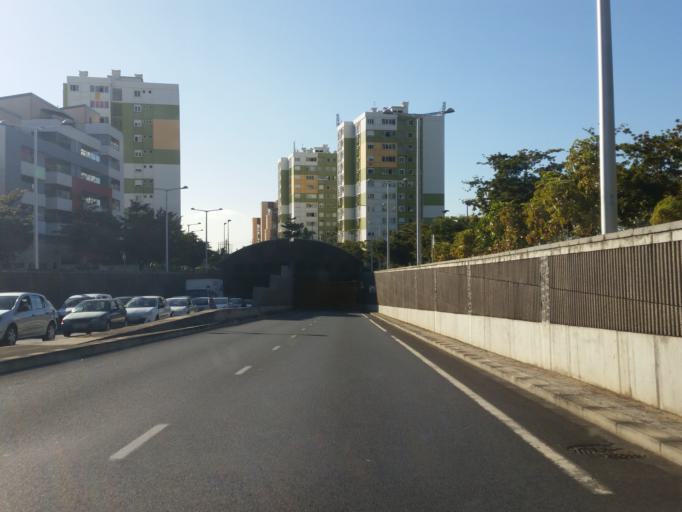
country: RE
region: Reunion
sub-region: Reunion
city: Saint-Denis
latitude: -20.8909
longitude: 55.4563
